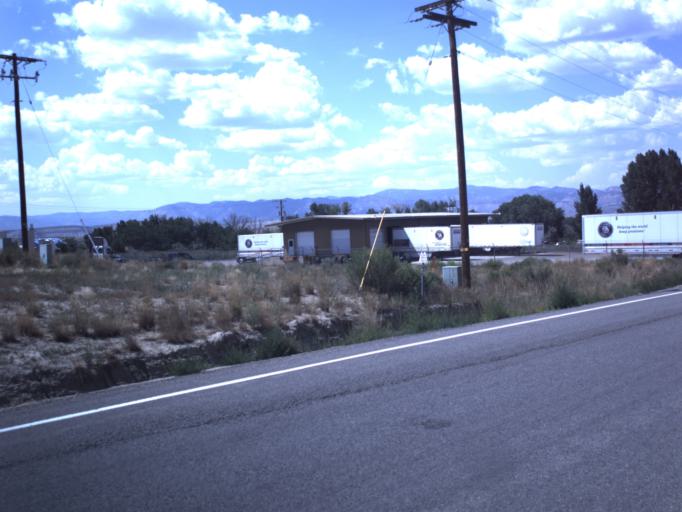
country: US
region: Utah
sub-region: Carbon County
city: Price
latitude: 39.5567
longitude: -110.8158
